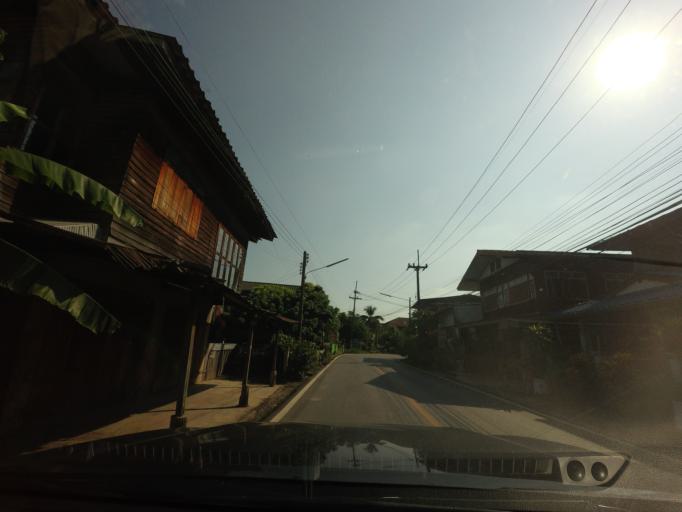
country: TH
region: Nan
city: Nan
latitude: 18.8570
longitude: 100.8115
